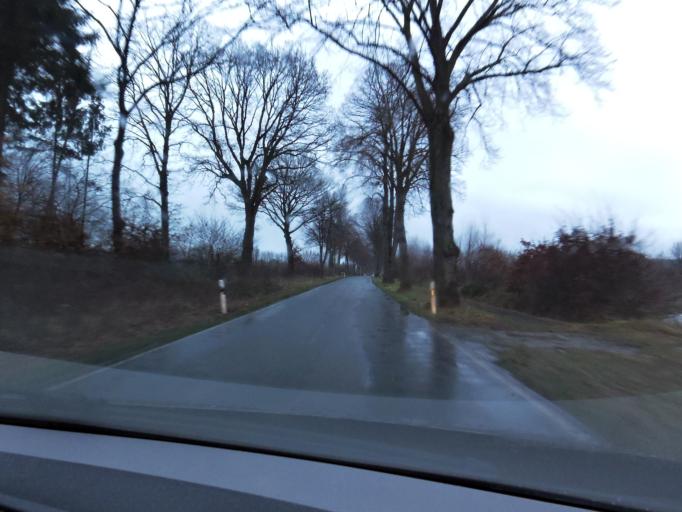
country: DE
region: Schleswig-Holstein
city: Salem
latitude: 53.6575
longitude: 10.8121
